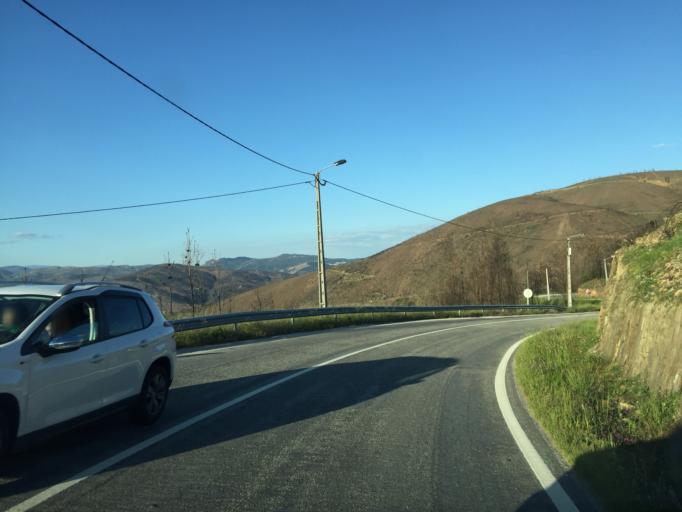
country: PT
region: Coimbra
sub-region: Pampilhosa da Serra
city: Pampilhosa da Serra
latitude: 40.0283
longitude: -7.9670
